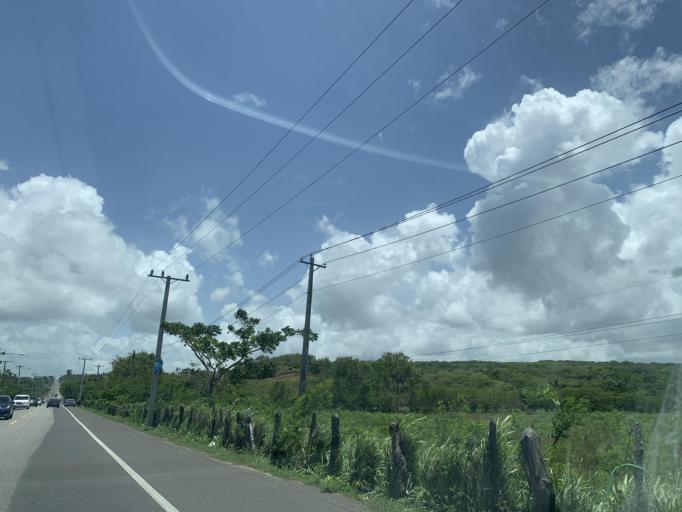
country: DO
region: Puerto Plata
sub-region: Puerto Plata
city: Puerto Plata
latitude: 19.7437
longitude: -70.6354
